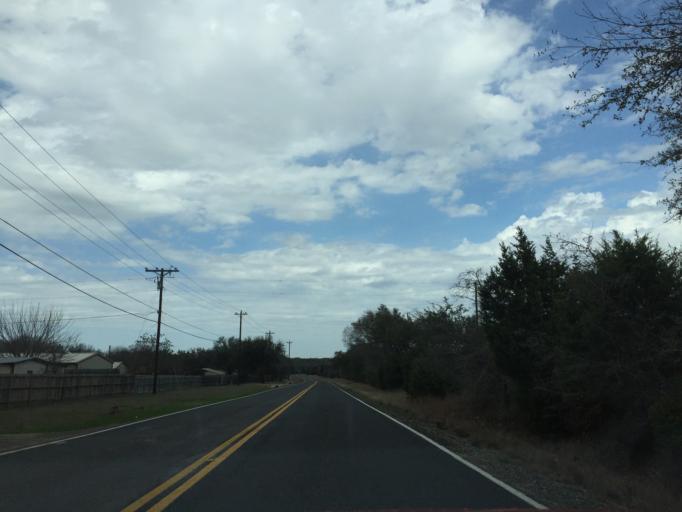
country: US
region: Texas
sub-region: Burnet County
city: Bertram
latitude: 30.7065
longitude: -97.9283
